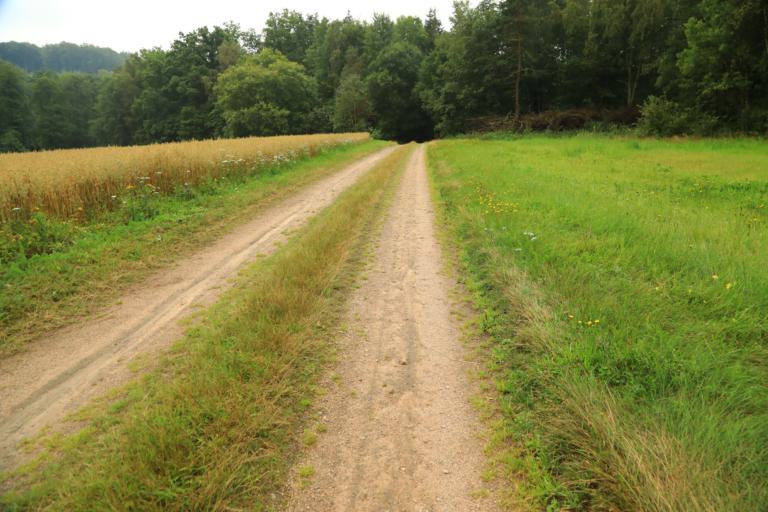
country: SE
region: Halland
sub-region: Falkenbergs Kommun
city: Falkenberg
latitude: 57.1136
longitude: 12.6846
